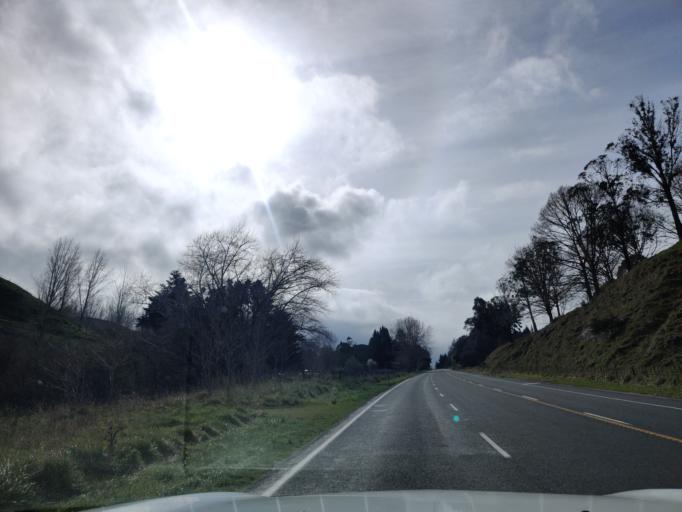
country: NZ
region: Manawatu-Wanganui
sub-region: Ruapehu District
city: Waiouru
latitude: -39.7746
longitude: 175.7910
